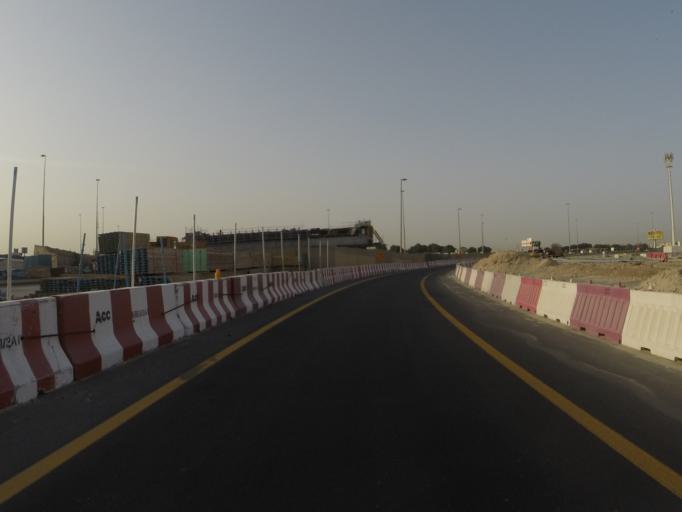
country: AE
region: Dubai
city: Dubai
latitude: 25.1691
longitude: 55.2659
